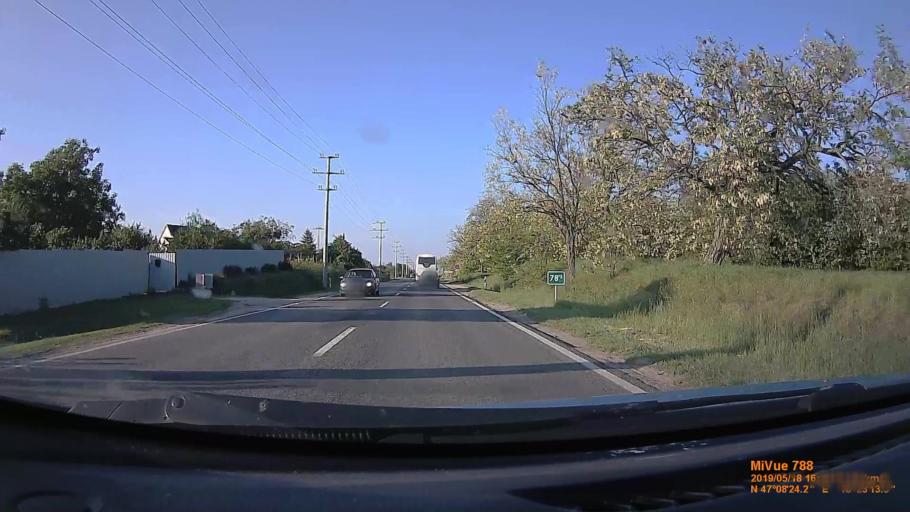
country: HU
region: Fejer
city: Szabadbattyan
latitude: 47.1402
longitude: 18.3872
